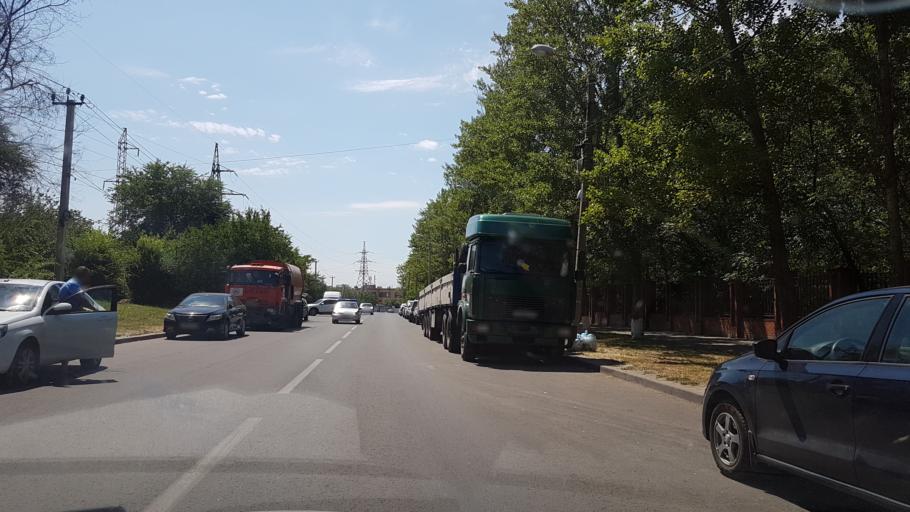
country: RU
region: Rostov
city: Severnyy
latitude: 47.2719
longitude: 39.7097
